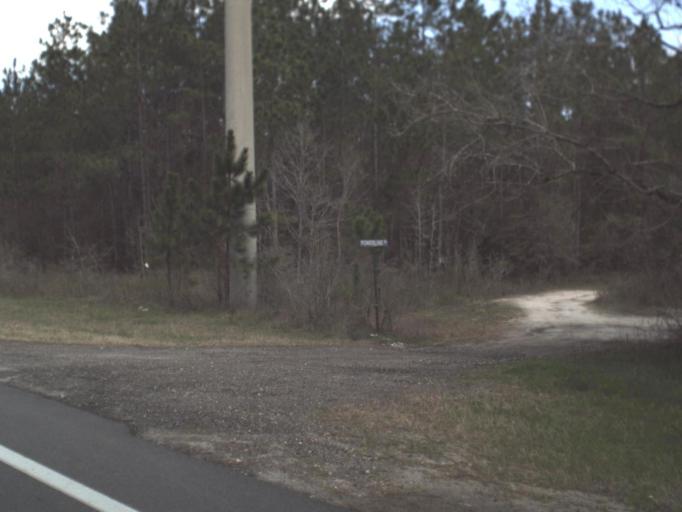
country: US
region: Florida
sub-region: Wakulla County
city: Crawfordville
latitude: 30.2489
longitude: -84.3623
